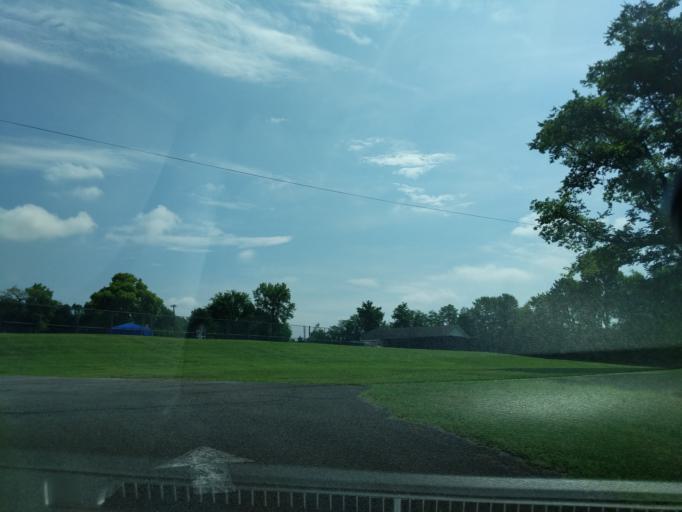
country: US
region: Tennessee
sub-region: Davidson County
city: Goodlettsville
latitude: 36.3046
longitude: -86.7094
